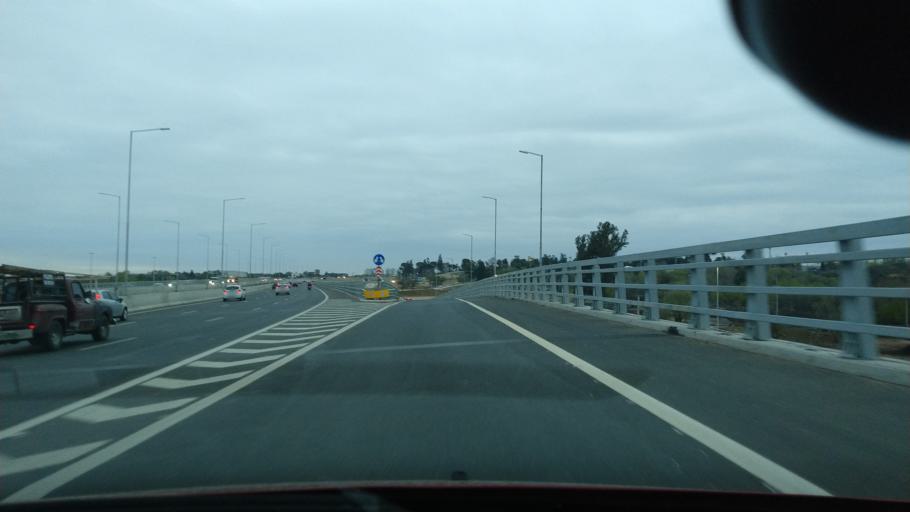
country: AR
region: Cordoba
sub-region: Departamento de Capital
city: Cordoba
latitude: -31.3669
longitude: -64.2505
